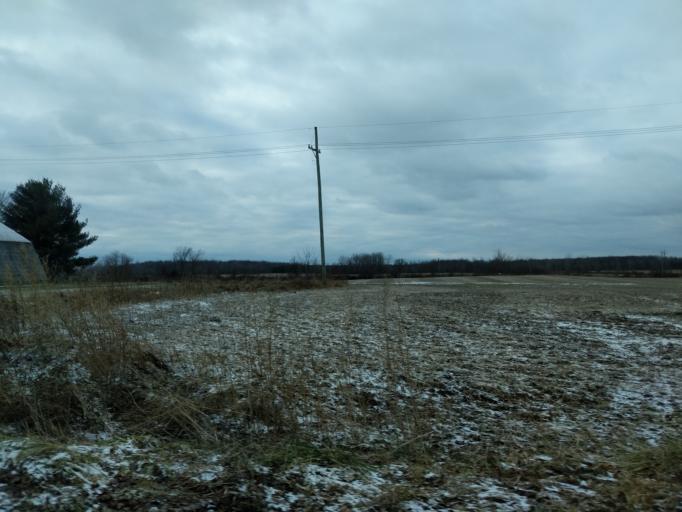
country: US
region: Michigan
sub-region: Lapeer County
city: North Branch
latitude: 43.3244
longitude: -83.1795
